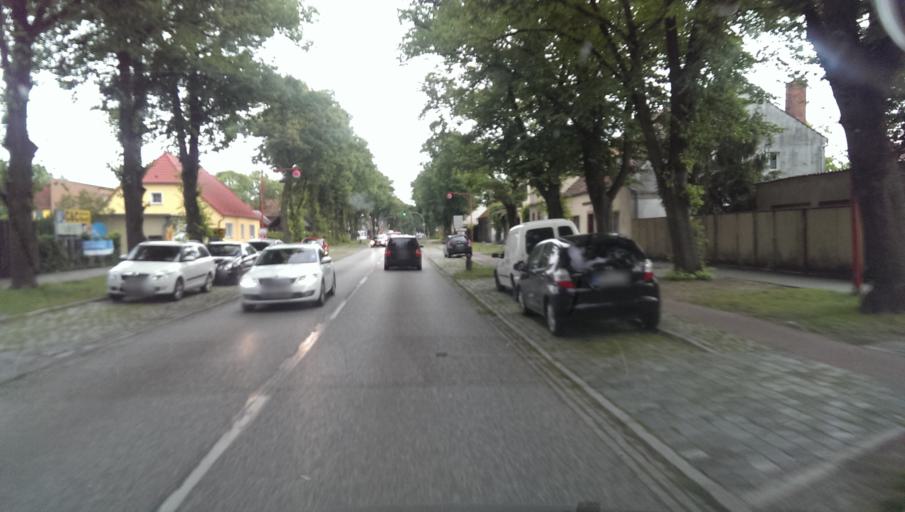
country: DE
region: Brandenburg
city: Premnitz
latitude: 52.5350
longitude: 12.3289
